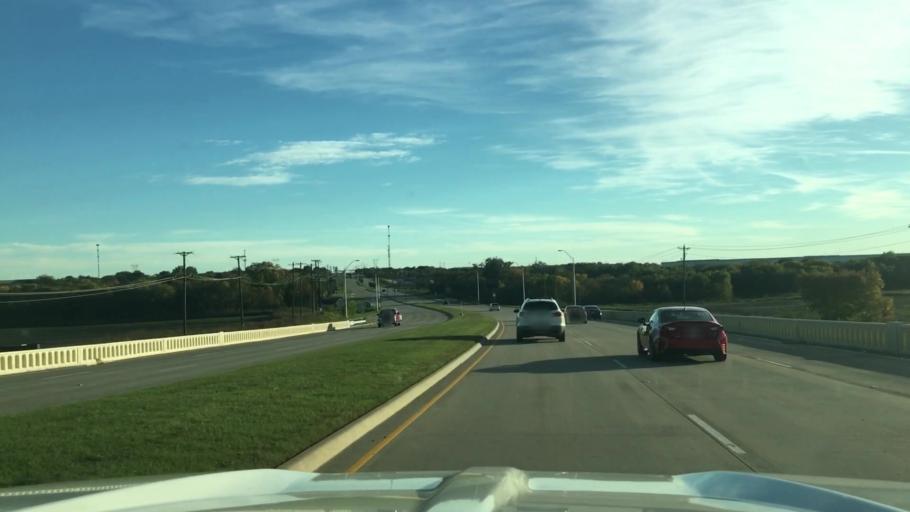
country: US
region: Texas
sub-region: Collin County
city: Prosper
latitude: 33.2177
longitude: -96.8023
